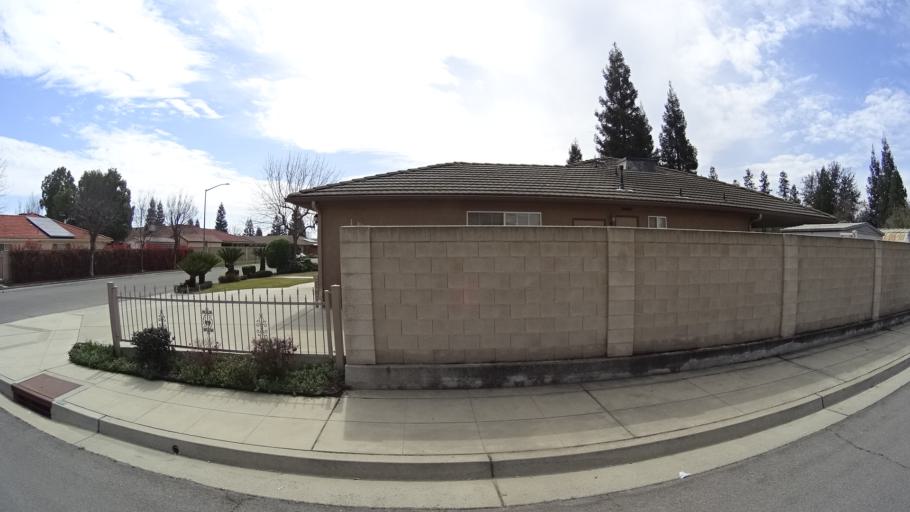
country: US
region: California
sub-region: Fresno County
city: Biola
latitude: 36.8419
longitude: -119.8878
